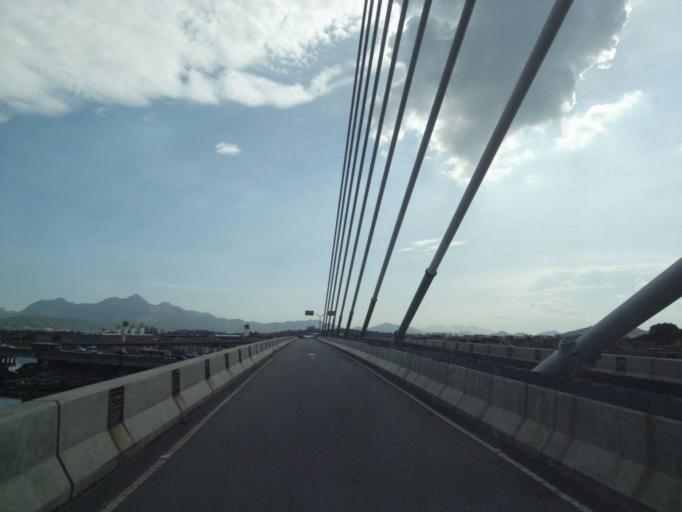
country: BR
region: Rio de Janeiro
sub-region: Rio De Janeiro
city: Rio de Janeiro
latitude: -22.8665
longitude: -43.2319
